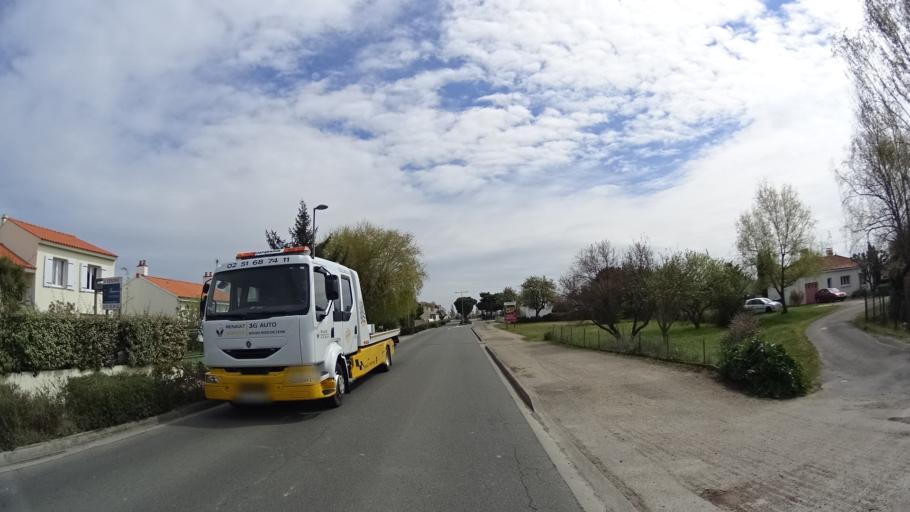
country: FR
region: Pays de la Loire
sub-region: Departement de la Vendee
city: La Barre-de-Monts
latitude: 46.8891
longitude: -2.1147
